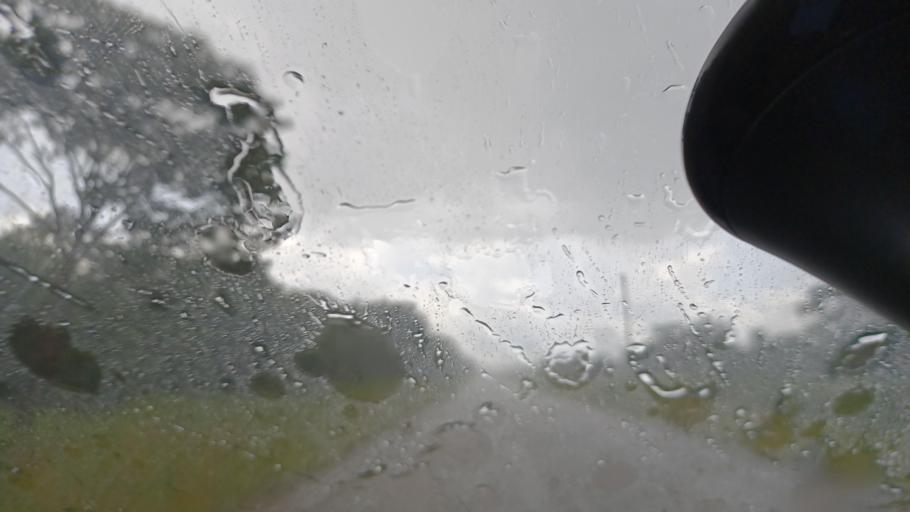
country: ZM
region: North-Western
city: Kasempa
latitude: -13.0952
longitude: 25.9142
